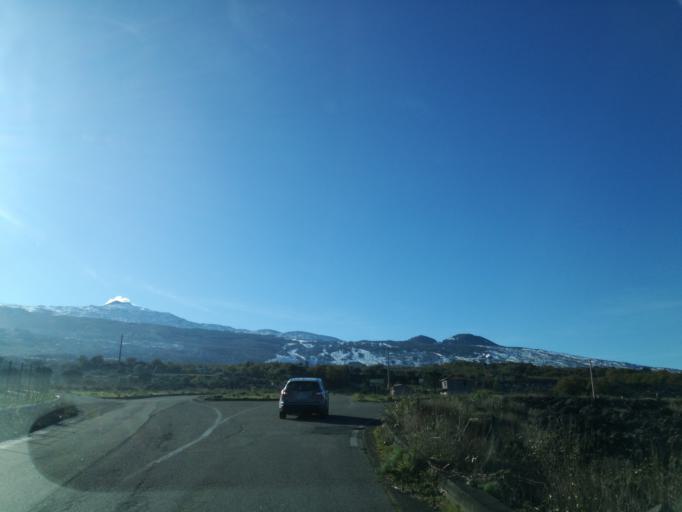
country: IT
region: Sicily
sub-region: Catania
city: Randazzo
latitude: 37.8669
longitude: 14.9797
